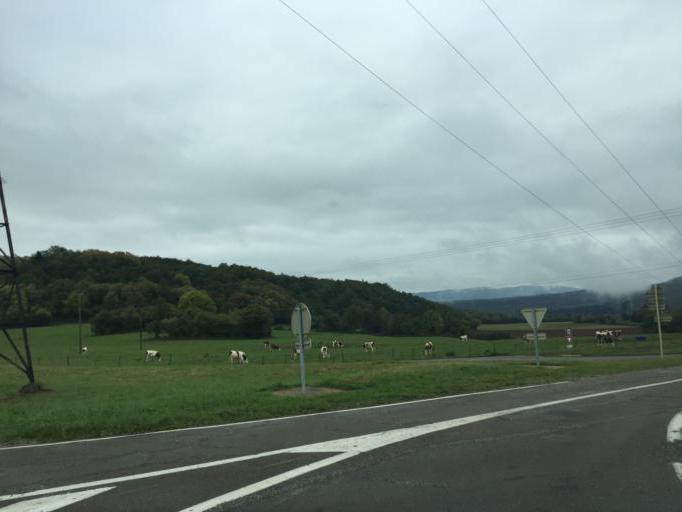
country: FR
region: Franche-Comte
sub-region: Departement du Jura
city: Orgelet
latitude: 46.5264
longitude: 5.6323
